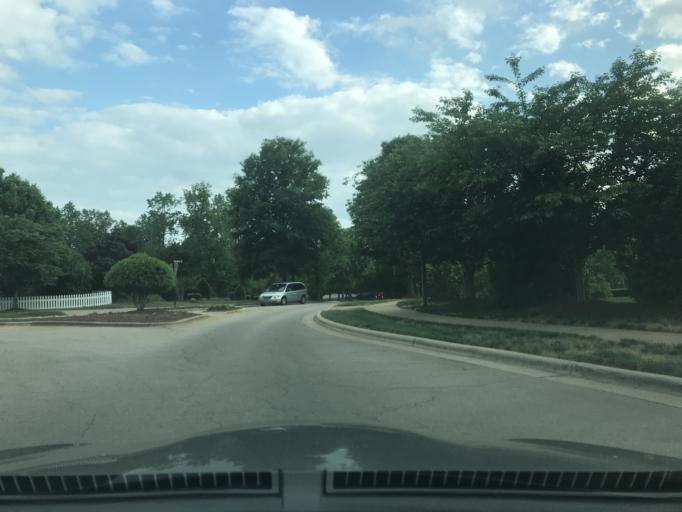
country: US
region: North Carolina
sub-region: Wake County
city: Wake Forest
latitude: 35.9230
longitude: -78.5636
